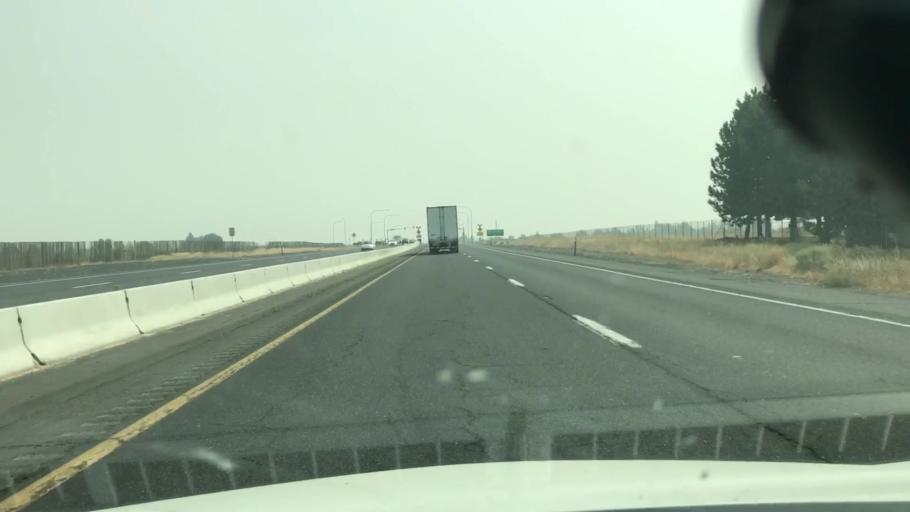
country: US
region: Washington
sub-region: Grant County
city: Cascade Valley
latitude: 47.1582
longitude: -119.3160
